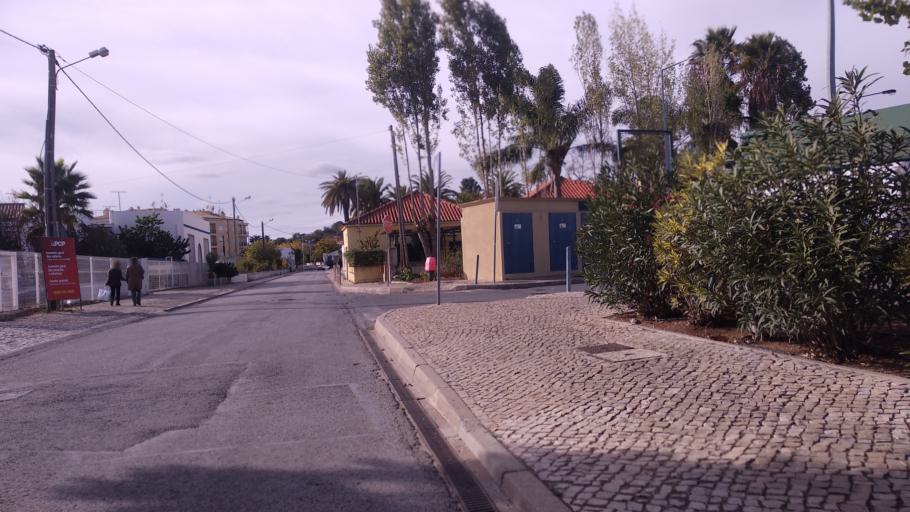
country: PT
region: Faro
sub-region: Sao Bras de Alportel
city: Sao Bras de Alportel
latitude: 37.1529
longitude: -7.8934
